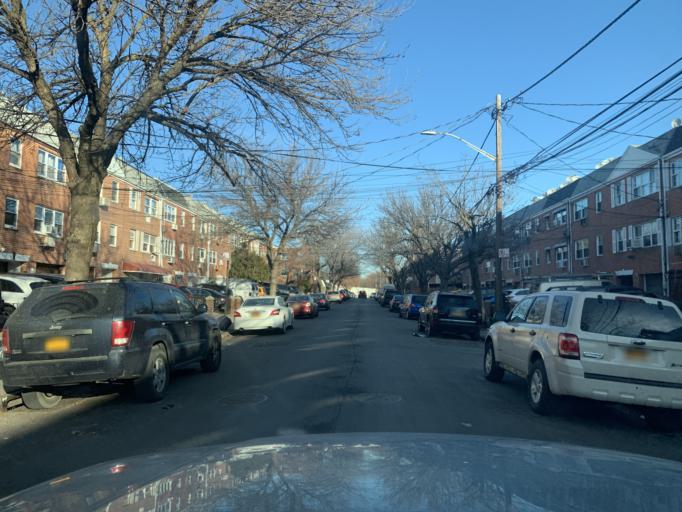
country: US
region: New York
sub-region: Queens County
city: Long Island City
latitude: 40.7589
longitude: -73.8973
